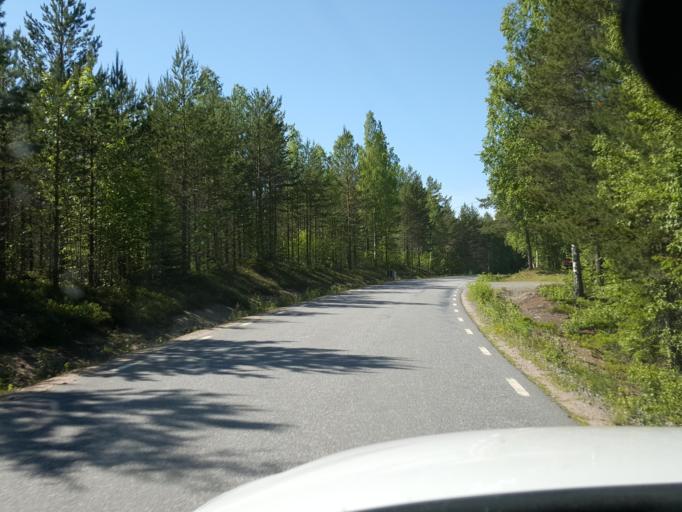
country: SE
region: Gaevleborg
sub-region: Ljusdals Kommun
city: Jaervsoe
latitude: 61.7506
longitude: 16.2367
